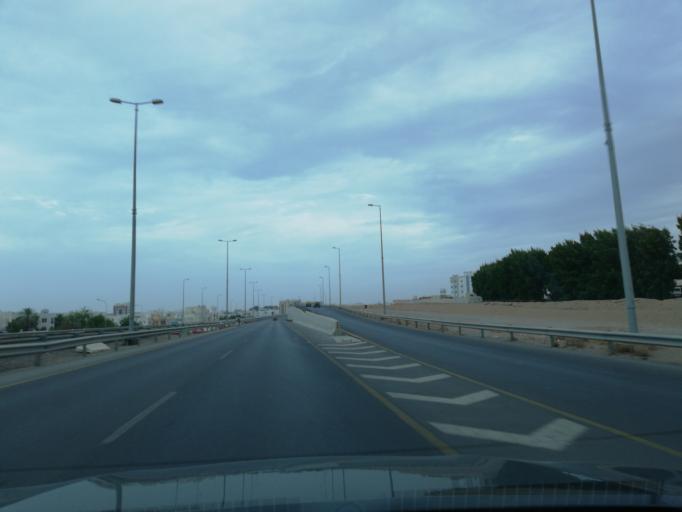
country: OM
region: Muhafazat Masqat
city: Bawshar
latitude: 23.5894
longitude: 58.4388
